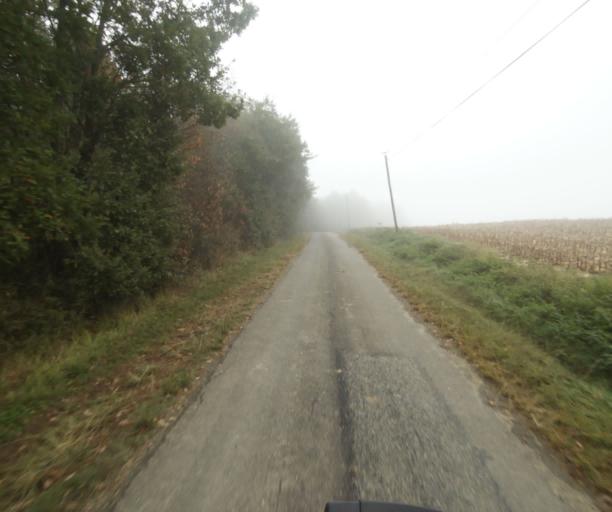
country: FR
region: Midi-Pyrenees
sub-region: Departement du Tarn-et-Garonne
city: Nohic
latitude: 43.9090
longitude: 1.4723
